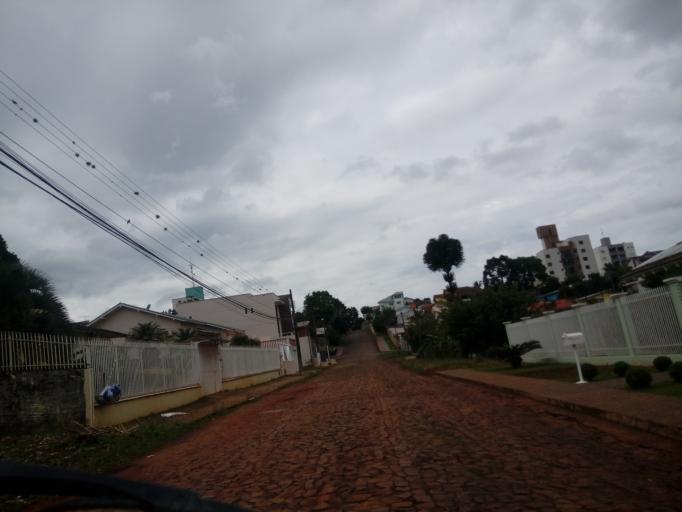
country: BR
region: Santa Catarina
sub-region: Chapeco
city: Chapeco
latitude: -27.0764
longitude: -52.6180
